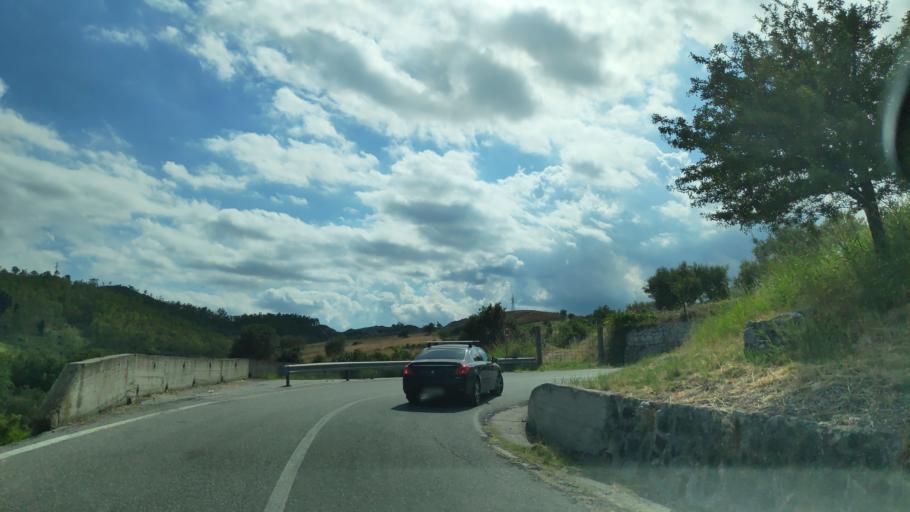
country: IT
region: Calabria
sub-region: Provincia di Catanzaro
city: Santa Caterina dello Ionio Marina
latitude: 38.5273
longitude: 16.5514
